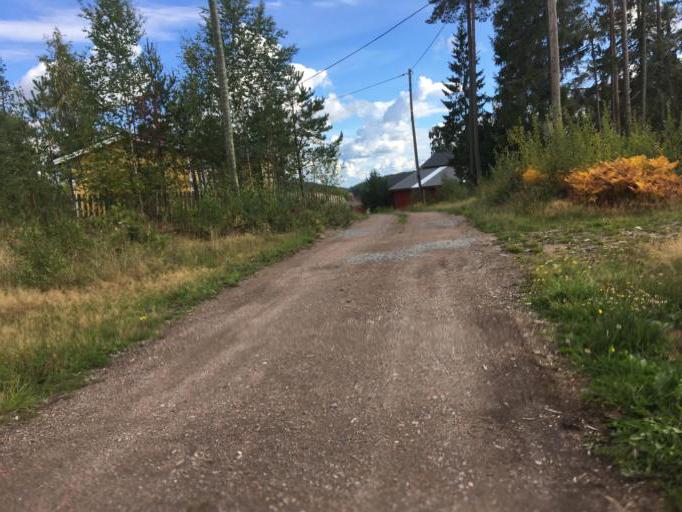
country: SE
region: Soedermanland
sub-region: Eskilstuna Kommun
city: Arla
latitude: 59.4542
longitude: 16.6643
